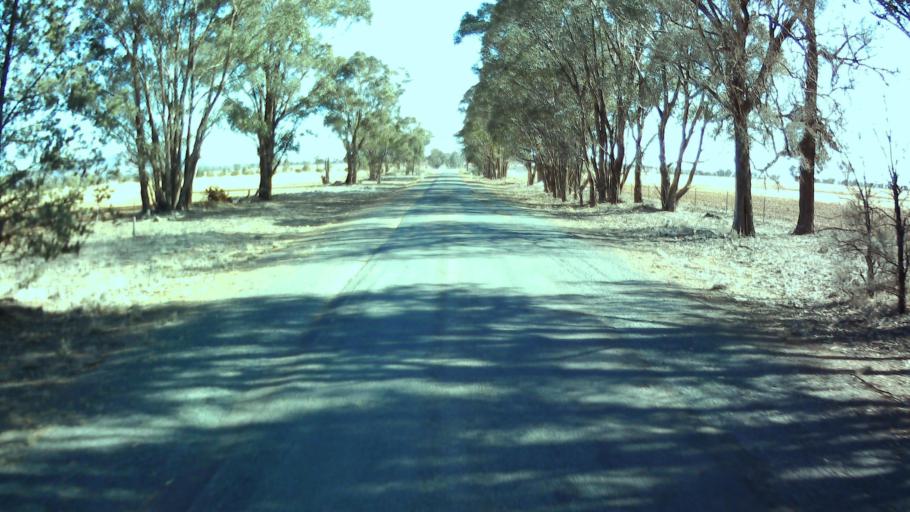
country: AU
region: New South Wales
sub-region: Weddin
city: Grenfell
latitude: -33.8022
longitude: 147.9555
